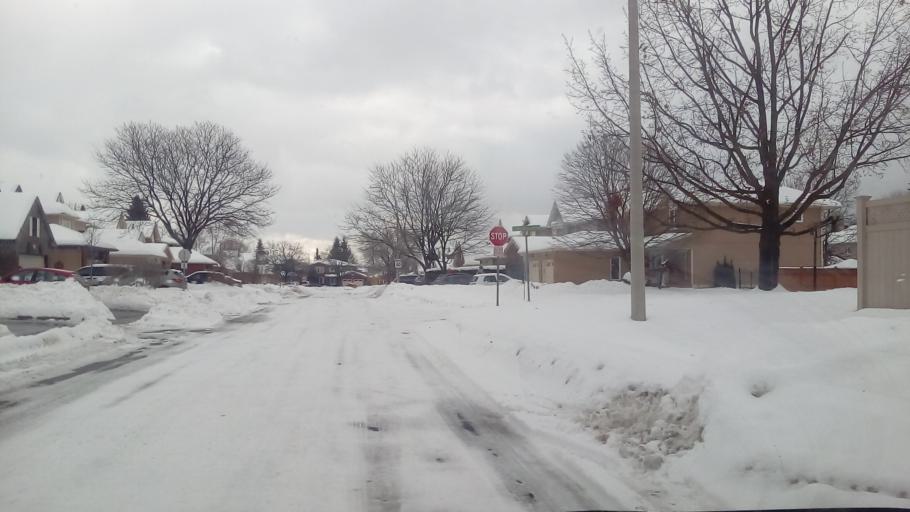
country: CA
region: Quebec
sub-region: Outaouais
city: Gatineau
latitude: 45.4571
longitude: -75.5287
